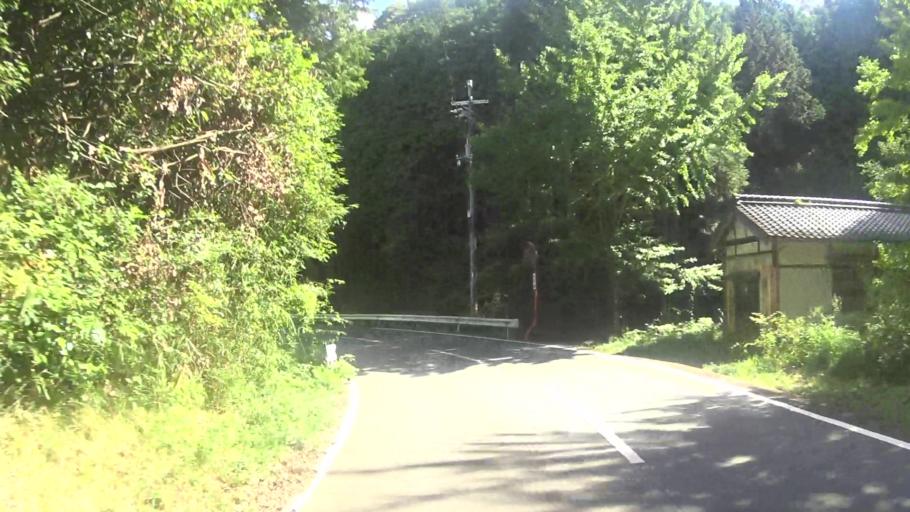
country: JP
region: Mie
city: Ueno-ebisumachi
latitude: 34.7372
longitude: 135.9988
